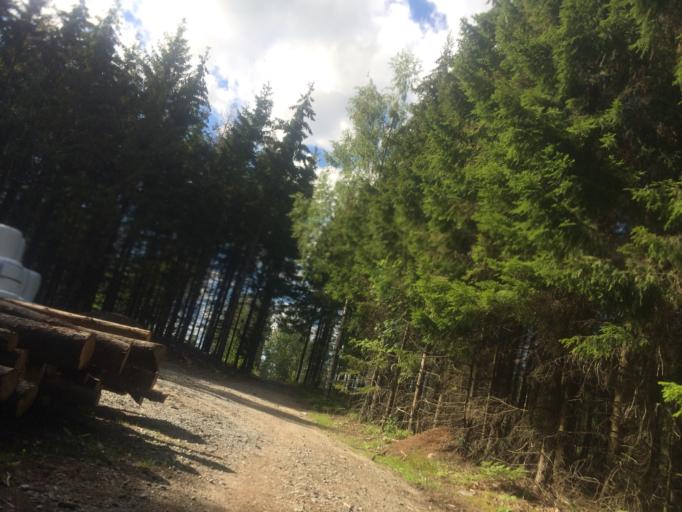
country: NO
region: Akershus
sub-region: As
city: As
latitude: 59.6734
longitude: 10.7896
